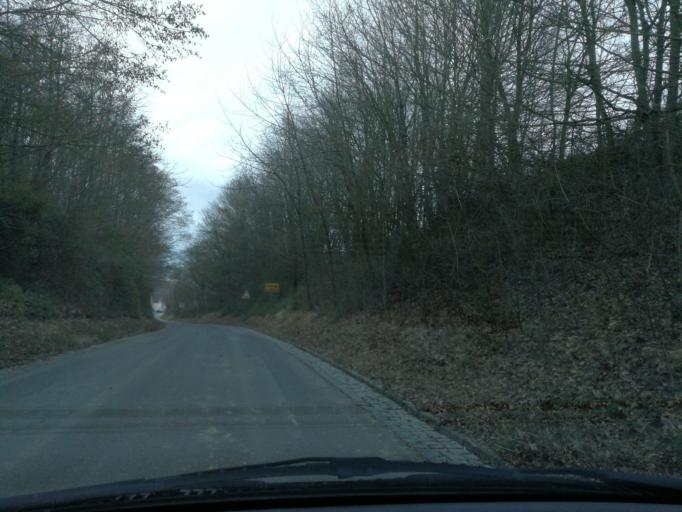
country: DE
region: Hesse
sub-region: Regierungsbezirk Darmstadt
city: Rossdorf
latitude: 49.8397
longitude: 8.7941
